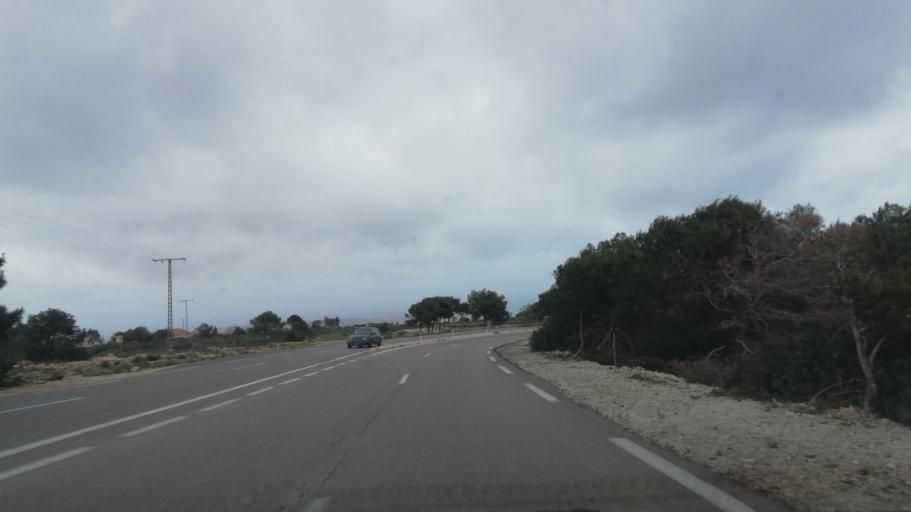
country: DZ
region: Oran
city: Mers el Kebir
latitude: 35.7181
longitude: -0.7411
